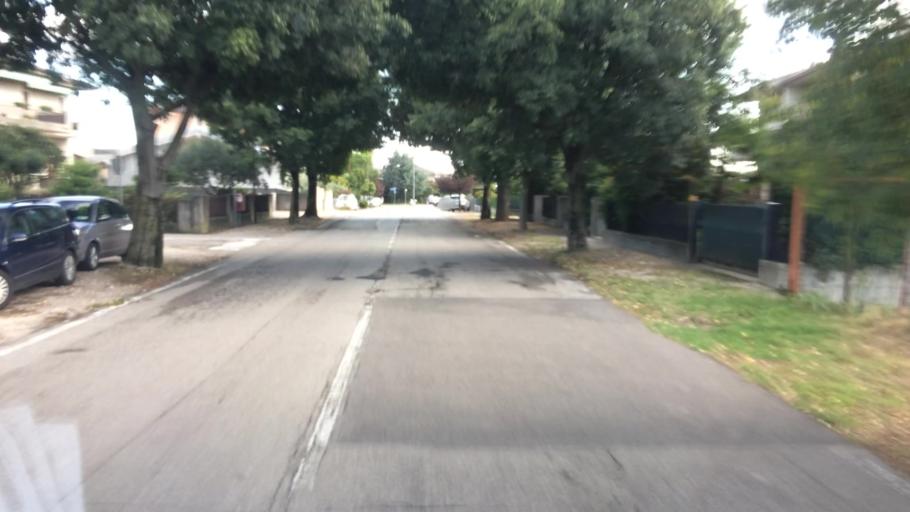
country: IT
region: Veneto
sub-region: Provincia di Verona
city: Bussolengo
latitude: 45.4650
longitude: 10.8642
